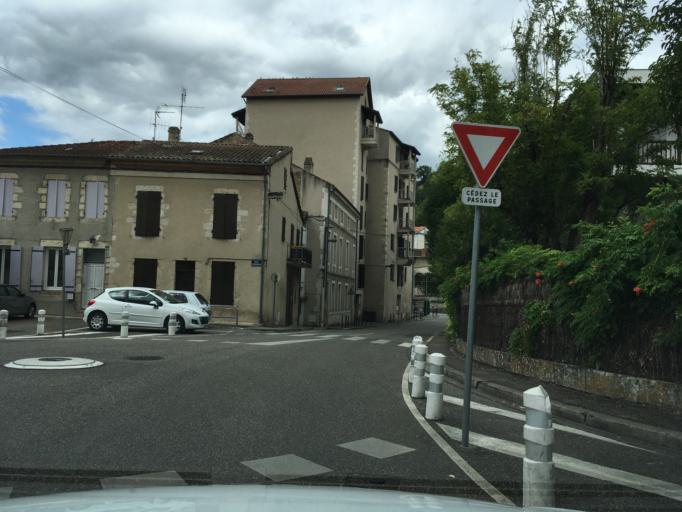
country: FR
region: Aquitaine
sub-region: Departement du Lot-et-Garonne
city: Le Passage
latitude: 44.2072
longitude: 0.6129
